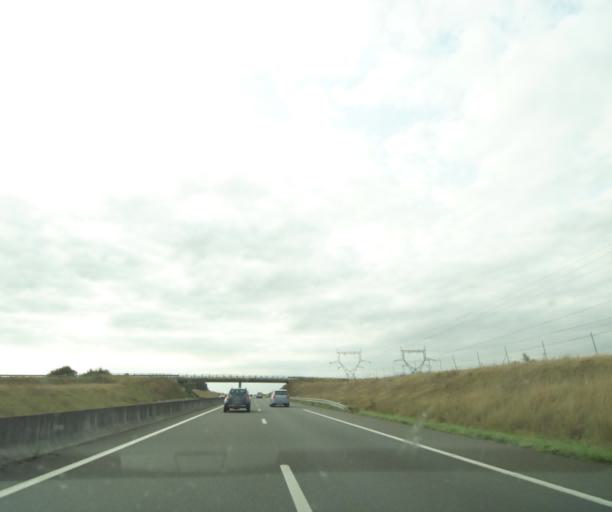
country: FR
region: Centre
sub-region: Departement d'Indre-et-Loire
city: Rouziers-de-Touraine
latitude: 47.4950
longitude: 0.6565
